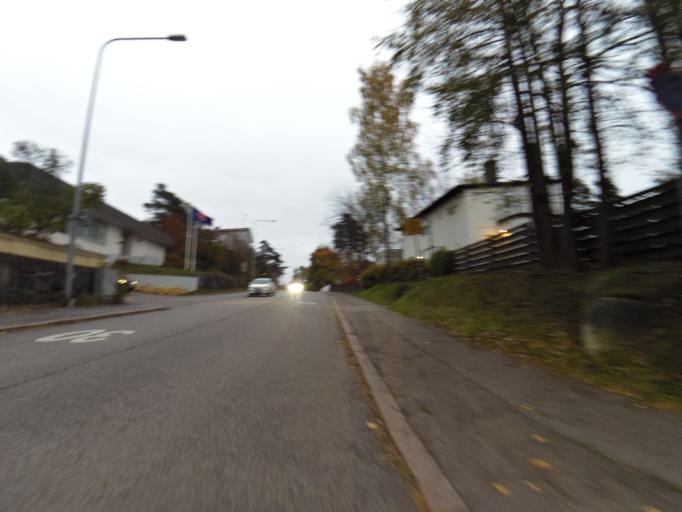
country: FI
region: Uusimaa
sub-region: Helsinki
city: Helsinki
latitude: 60.1846
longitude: 25.0035
